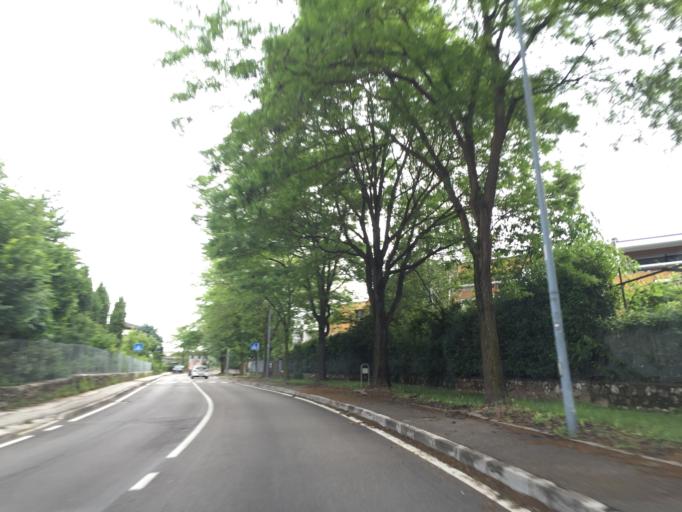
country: IT
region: Trentino-Alto Adige
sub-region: Provincia di Trento
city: Povo
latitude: 46.0463
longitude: 11.1418
